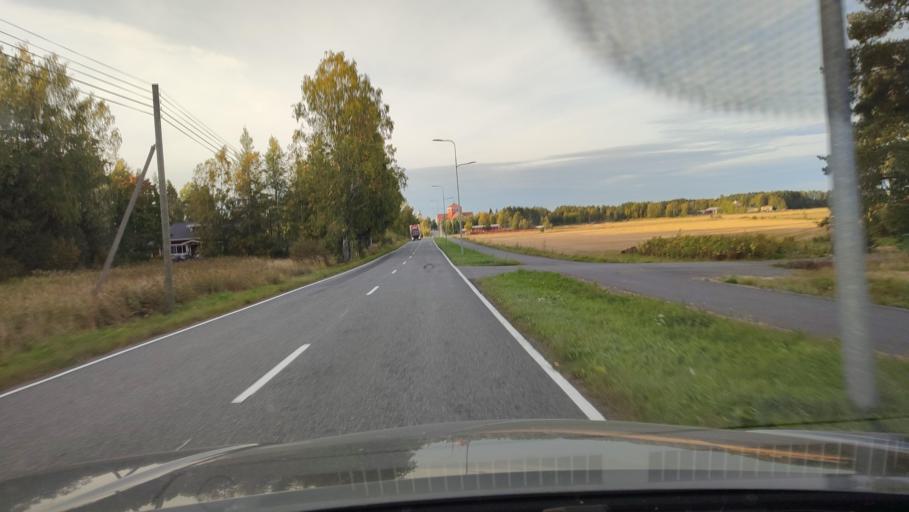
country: FI
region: Ostrobothnia
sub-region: Sydosterbotten
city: Kristinestad
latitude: 62.2388
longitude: 21.5209
